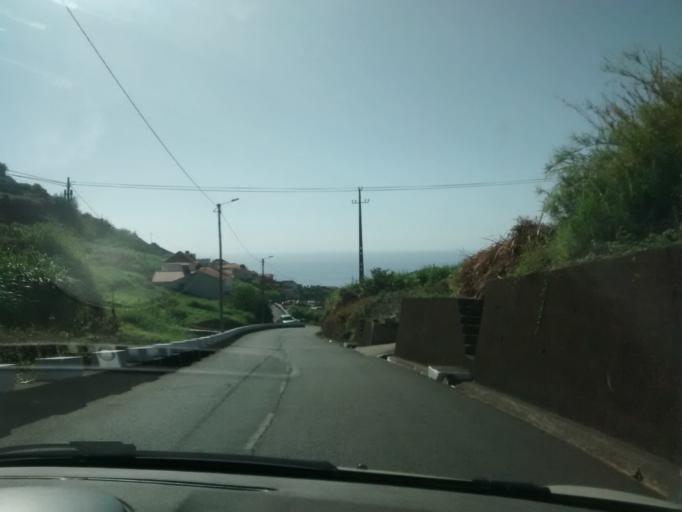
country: PT
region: Madeira
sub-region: Calheta
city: Arco da Calheta
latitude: 32.7257
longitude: -17.1653
